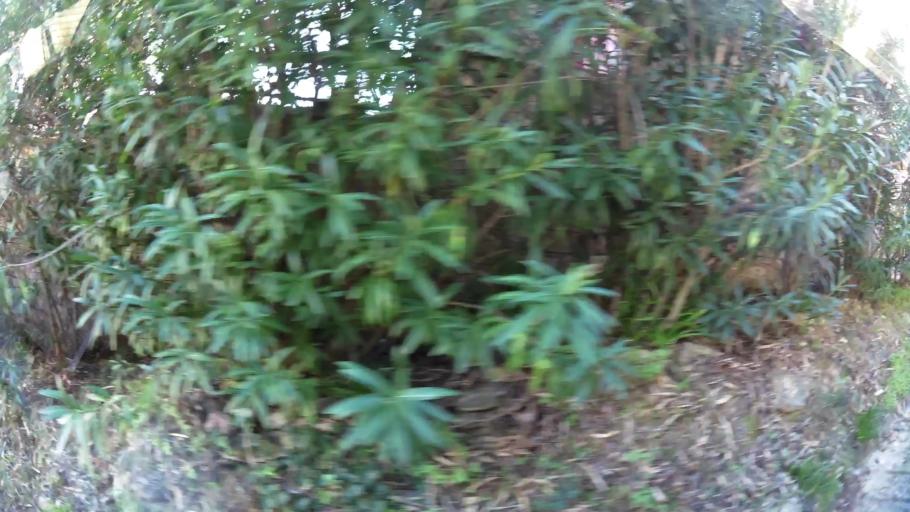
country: GR
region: Attica
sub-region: Nomarchia Anatolikis Attikis
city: Anoixi
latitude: 38.1274
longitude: 23.8606
